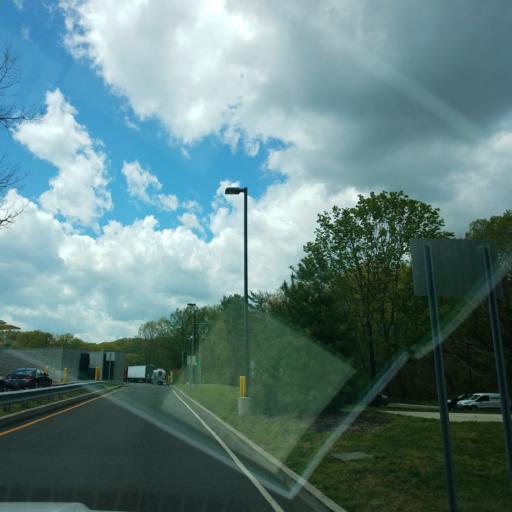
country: US
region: Connecticut
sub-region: New Haven County
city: Madison
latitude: 41.2923
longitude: -72.5795
